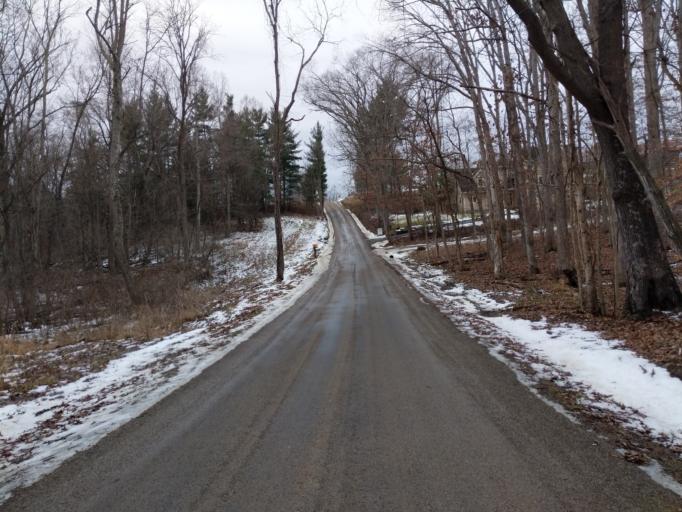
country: US
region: Ohio
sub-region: Athens County
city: The Plains
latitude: 39.3246
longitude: -82.1532
